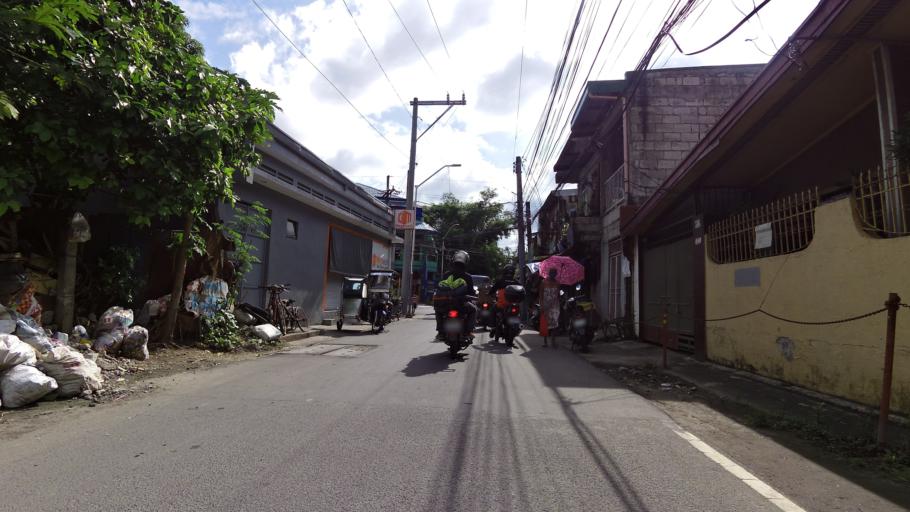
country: PH
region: Calabarzon
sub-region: Province of Rizal
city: Cainta
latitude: 14.5739
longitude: 121.1196
